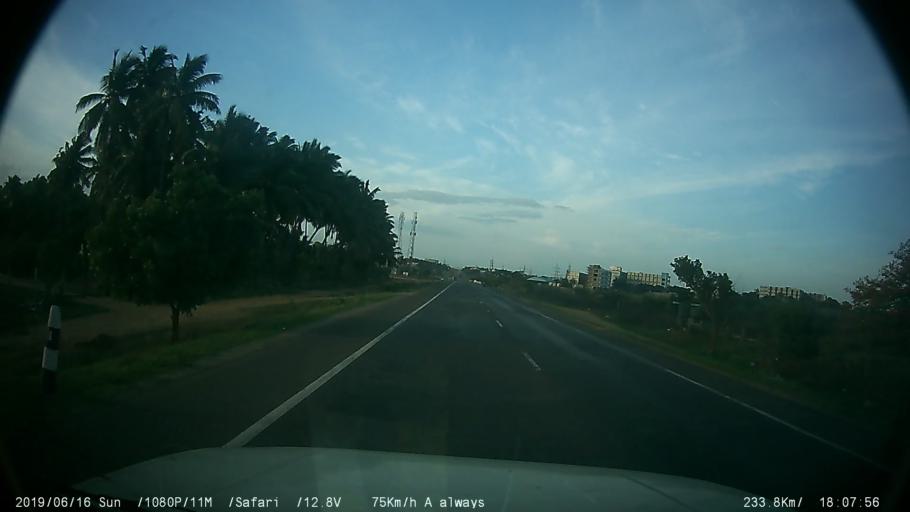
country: IN
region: Tamil Nadu
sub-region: Coimbatore
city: Madukkarai
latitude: 10.9055
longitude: 76.9748
